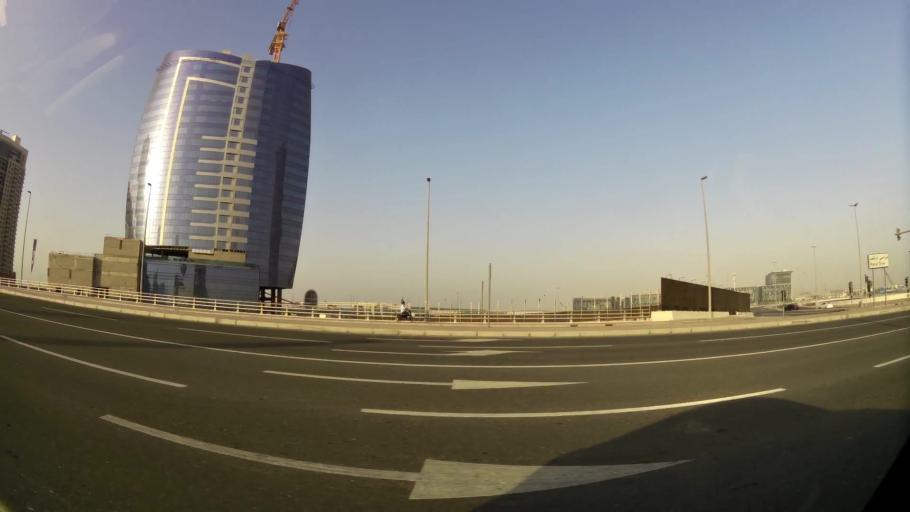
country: AE
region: Dubai
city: Dubai
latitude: 25.1901
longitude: 55.2895
